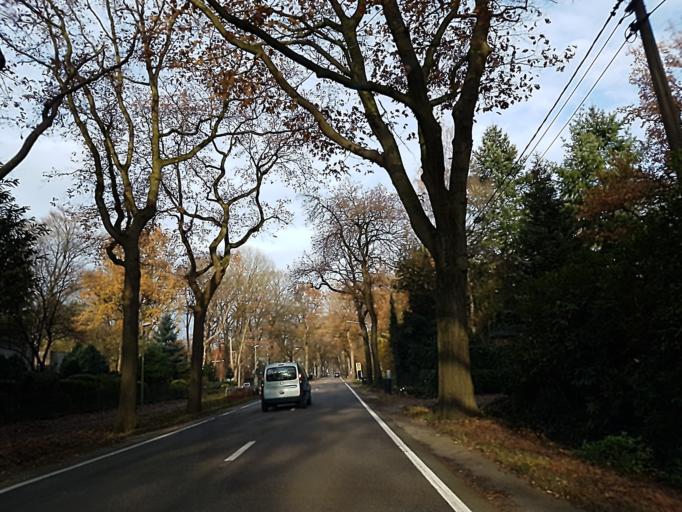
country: BE
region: Flanders
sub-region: Provincie Antwerpen
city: Essen
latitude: 51.4369
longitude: 4.4626
